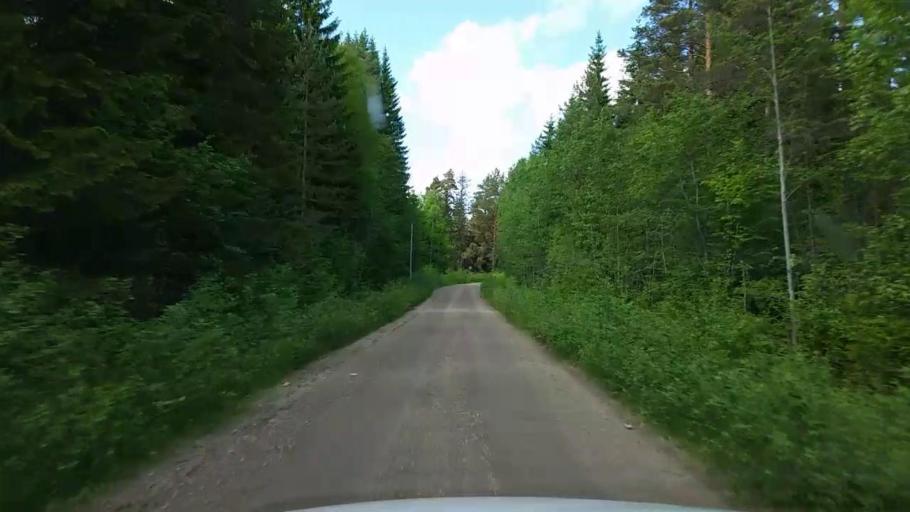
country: SE
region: Gaevleborg
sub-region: Ovanakers Kommun
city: Edsbyn
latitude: 61.5247
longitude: 15.9339
